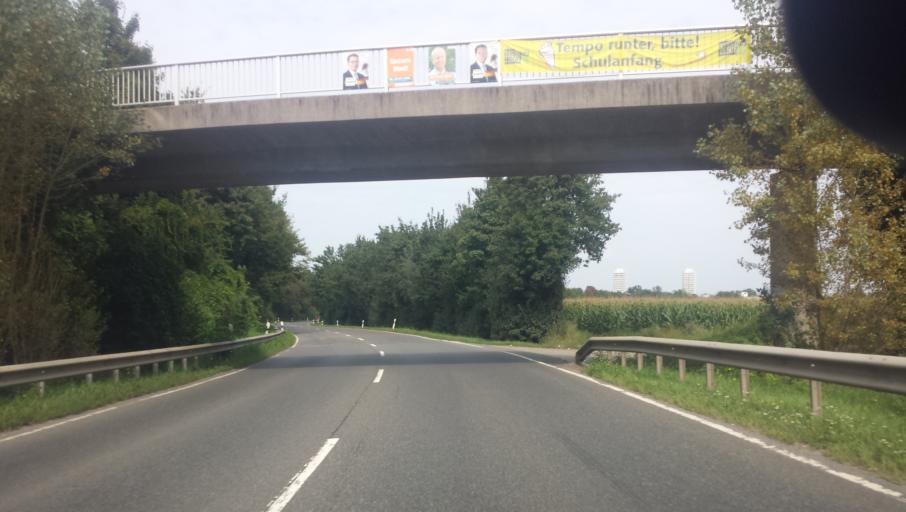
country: DE
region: Rheinland-Pfalz
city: Gartenstadt
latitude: 49.4819
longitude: 8.3799
